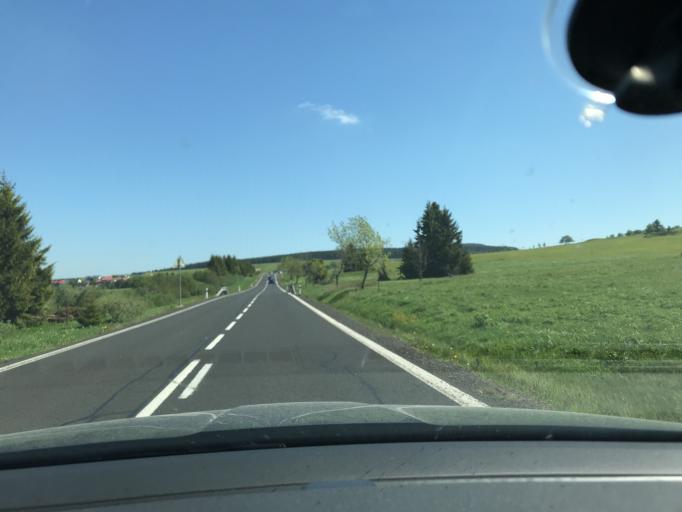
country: CZ
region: Karlovarsky
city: Jachymov
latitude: 50.4030
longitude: 12.9181
